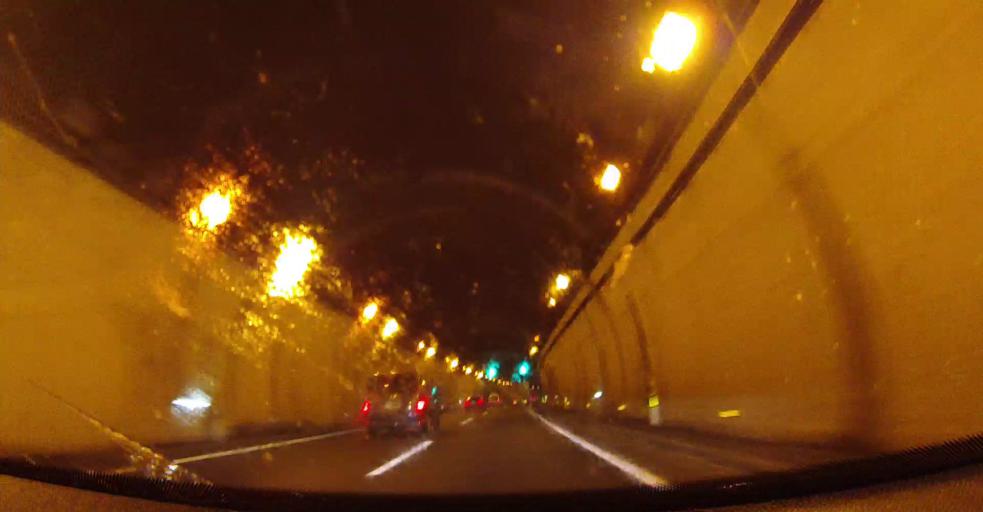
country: ES
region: Basque Country
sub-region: Provincia de Guipuzcoa
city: Getaria
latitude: 43.2813
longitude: -2.2083
